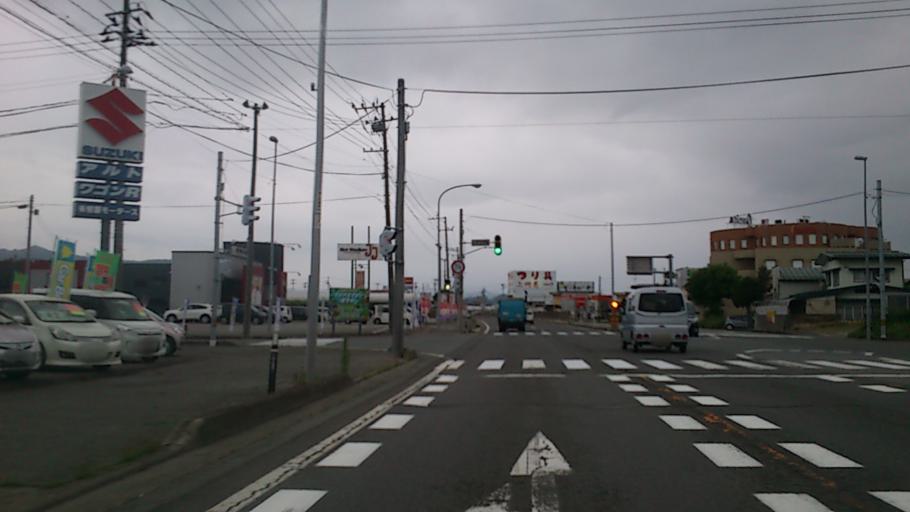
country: JP
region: Yamagata
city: Higashine
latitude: 38.4041
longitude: 140.3735
